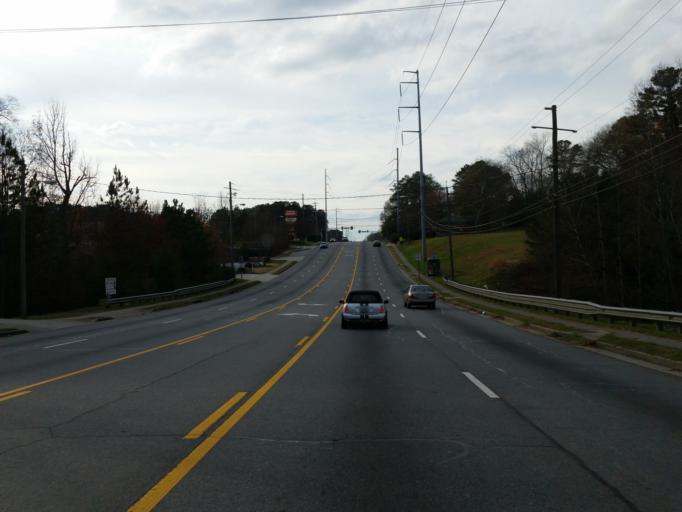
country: US
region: Georgia
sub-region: Cobb County
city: Fair Oaks
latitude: 33.8948
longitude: -84.5495
